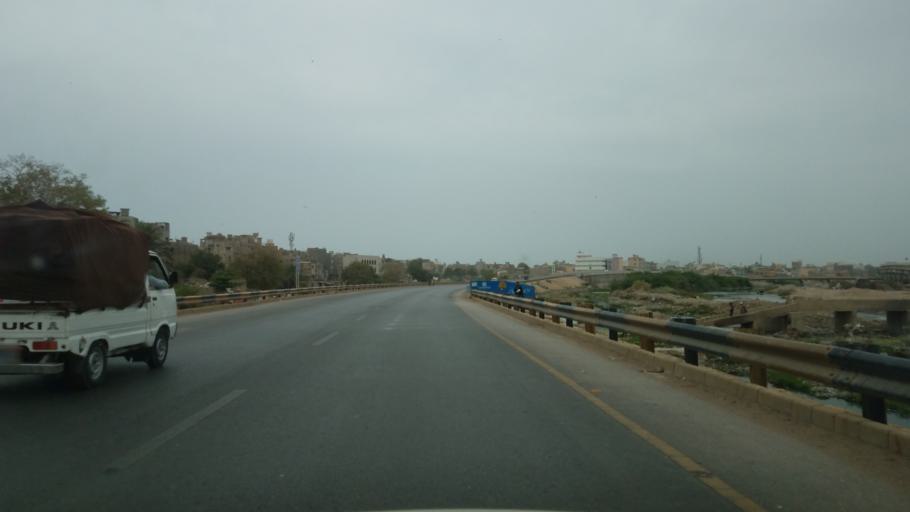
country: PK
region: Sindh
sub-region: Karachi District
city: Karachi
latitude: 24.8798
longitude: 67.0171
